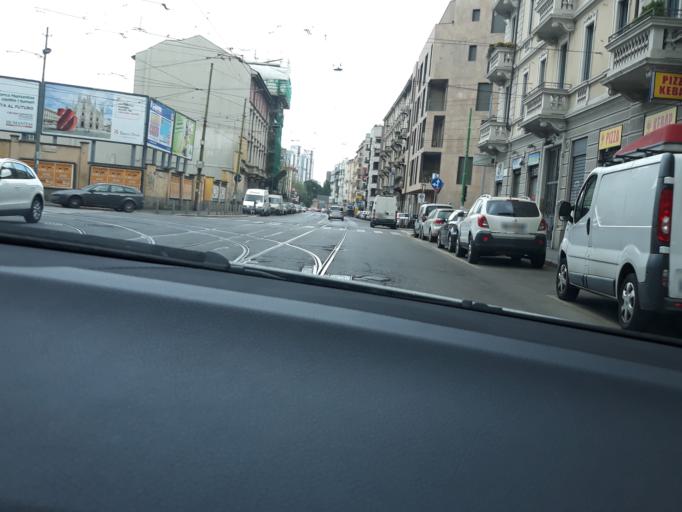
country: IT
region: Lombardy
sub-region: Citta metropolitana di Milano
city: Milano
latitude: 45.4837
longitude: 9.1718
